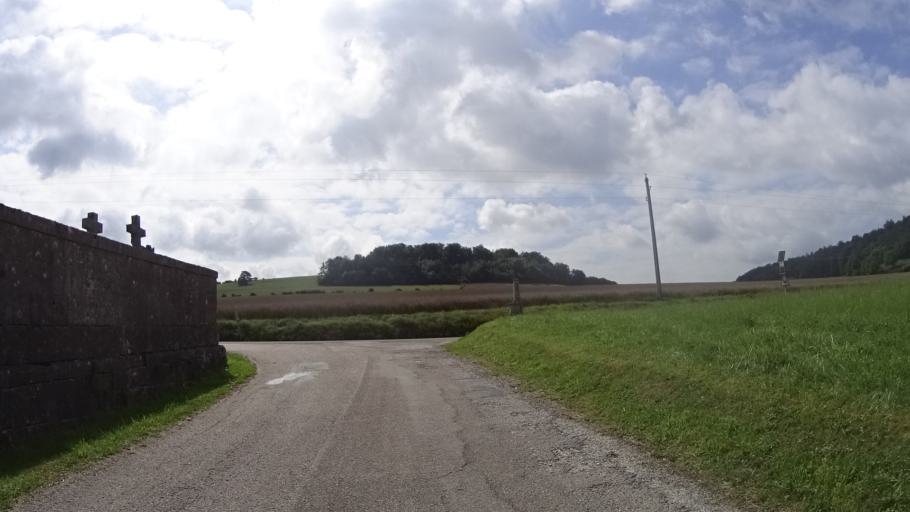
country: FR
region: Lorraine
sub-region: Departement de la Meuse
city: Ligny-en-Barrois
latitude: 48.7164
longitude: 5.3700
